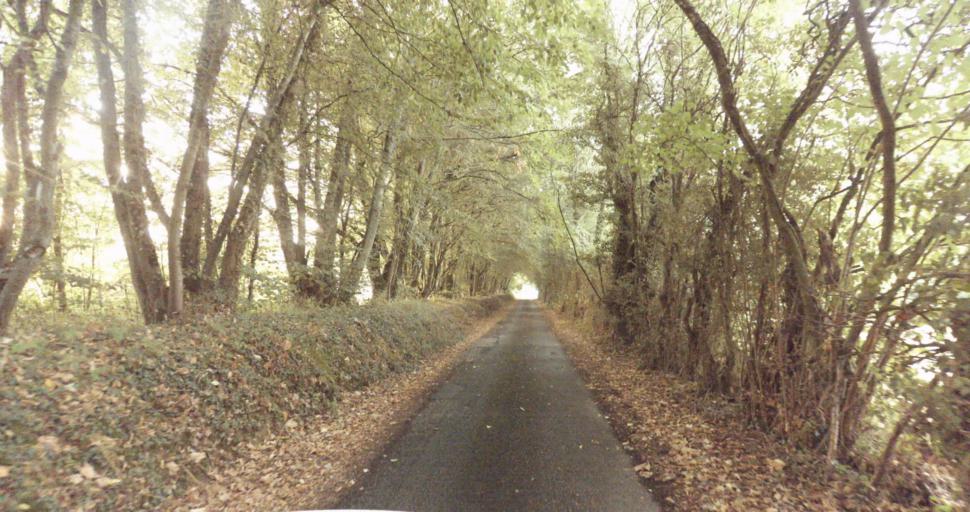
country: FR
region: Lower Normandy
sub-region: Departement de l'Orne
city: Vimoutiers
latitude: 48.9328
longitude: 0.2201
